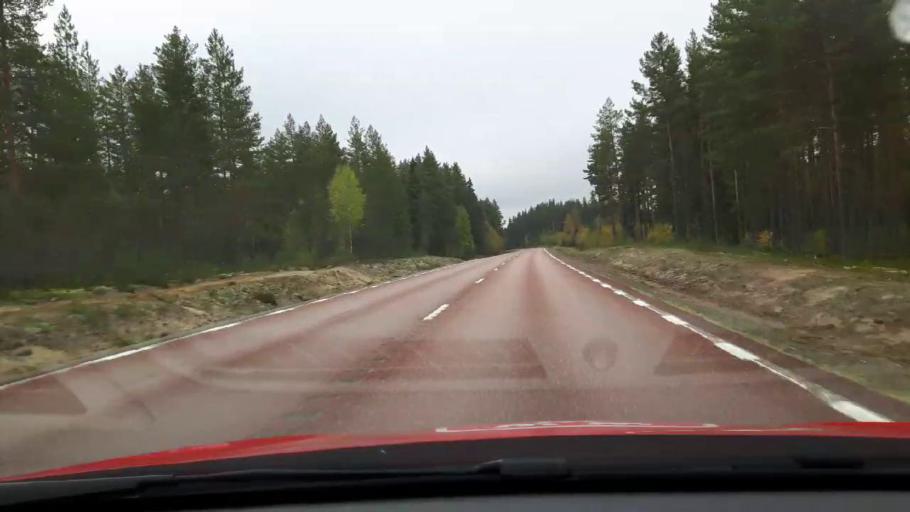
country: SE
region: Gaevleborg
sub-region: Ljusdals Kommun
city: Farila
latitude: 61.8241
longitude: 15.7558
